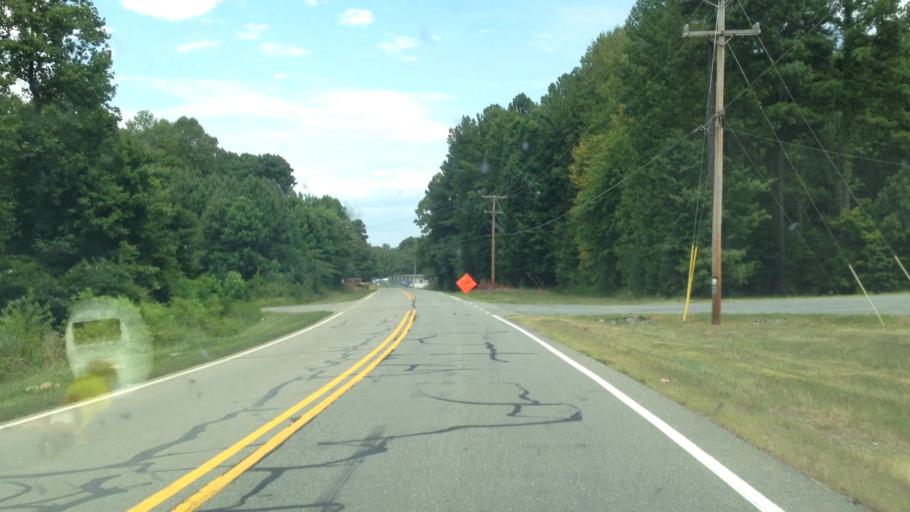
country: US
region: North Carolina
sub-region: Stokes County
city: Walnut Cove
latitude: 36.2831
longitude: -80.0696
